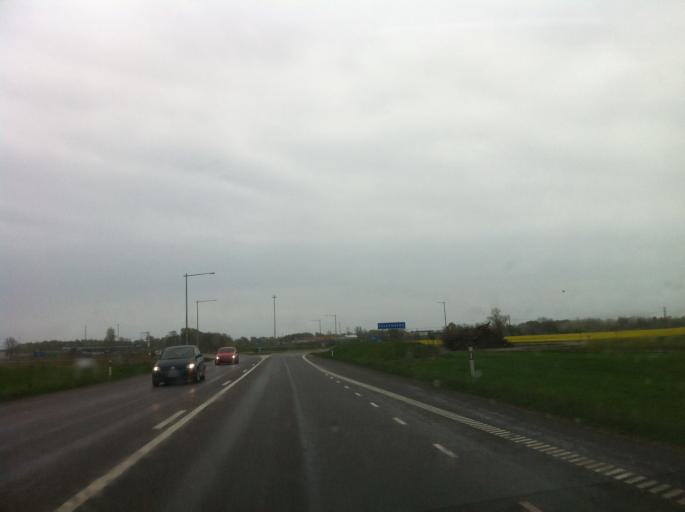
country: SE
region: Halland
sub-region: Falkenbergs Kommun
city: Falkenberg
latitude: 56.9246
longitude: 12.5091
